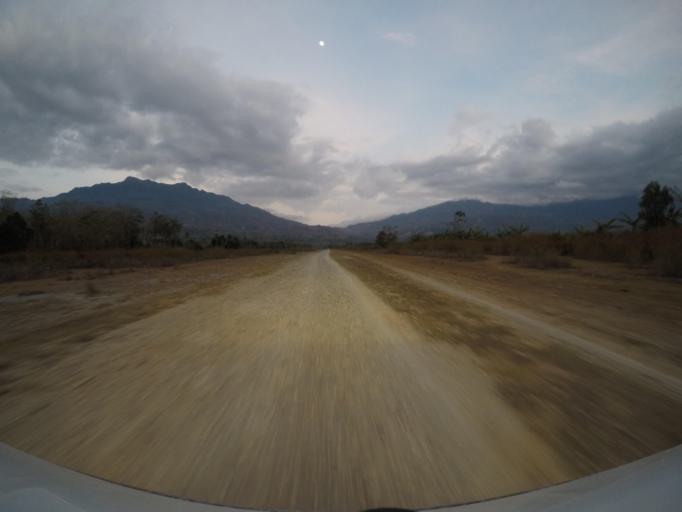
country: TL
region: Bobonaro
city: Maliana
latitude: -8.9715
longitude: 125.2132
